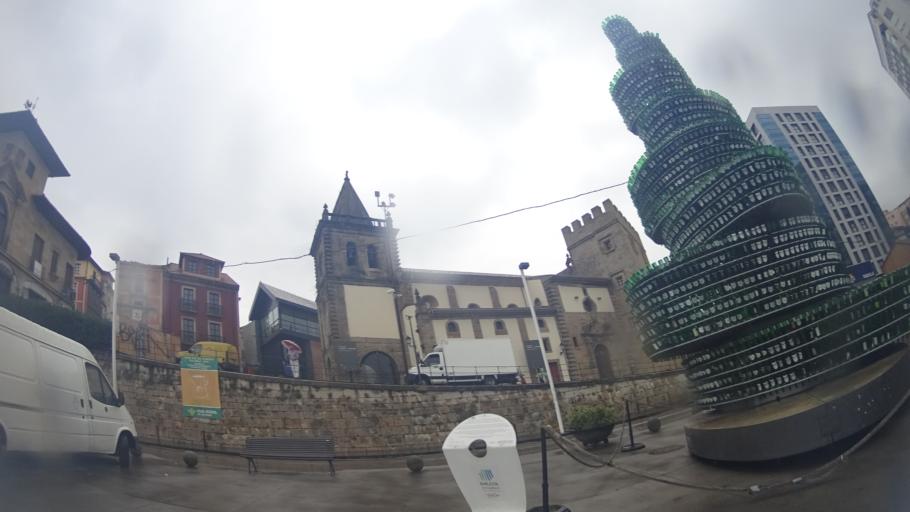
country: ES
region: Asturias
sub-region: Province of Asturias
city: Gijon
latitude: 43.5454
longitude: -5.6643
